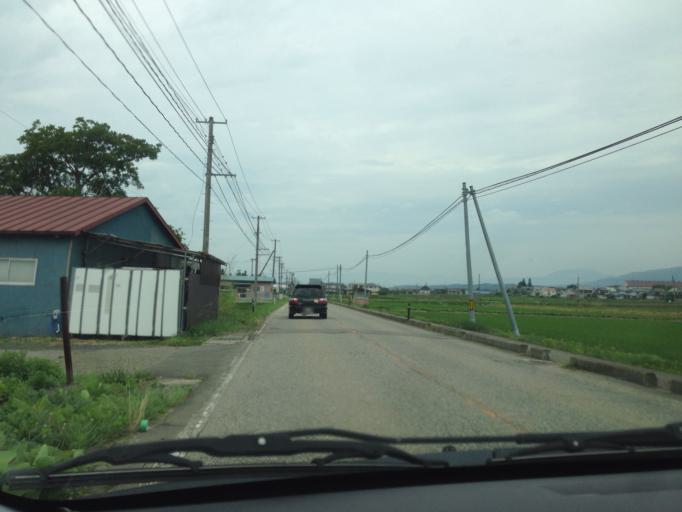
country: JP
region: Fukushima
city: Kitakata
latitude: 37.5388
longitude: 139.9295
